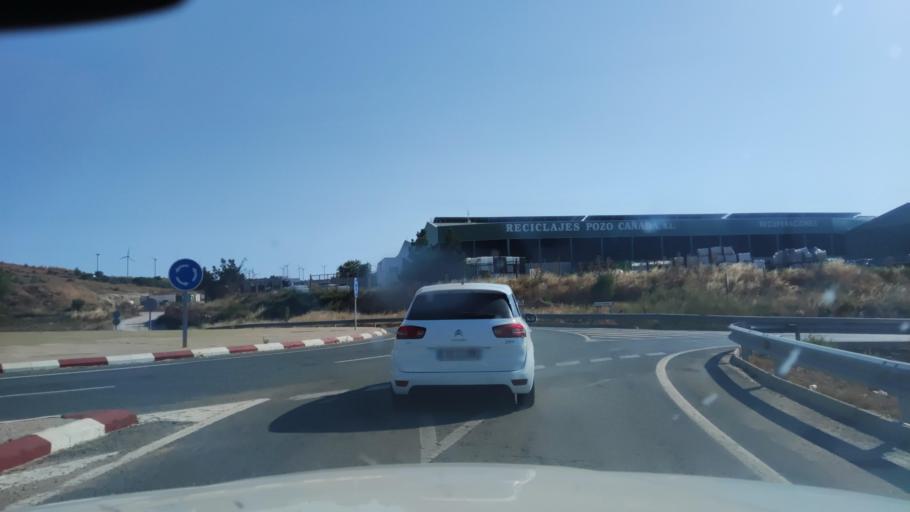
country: ES
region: Castille-La Mancha
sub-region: Provincia de Albacete
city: Pozo-Canada
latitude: 38.7926
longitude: -1.7263
